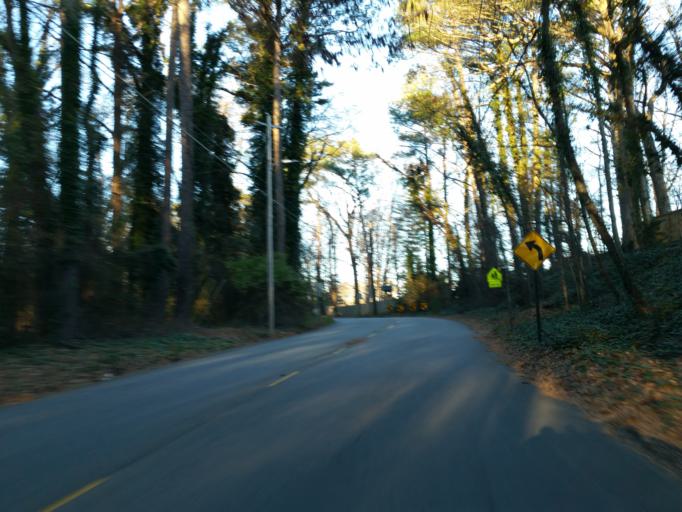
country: US
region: Georgia
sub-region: Cobb County
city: Vinings
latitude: 33.8413
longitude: -84.4080
